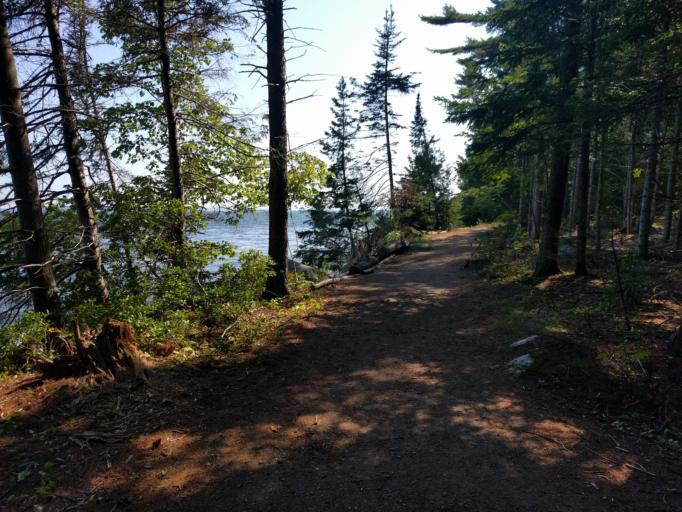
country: US
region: Maine
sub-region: Waldo County
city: Belfast
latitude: 44.4314
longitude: -68.9426
